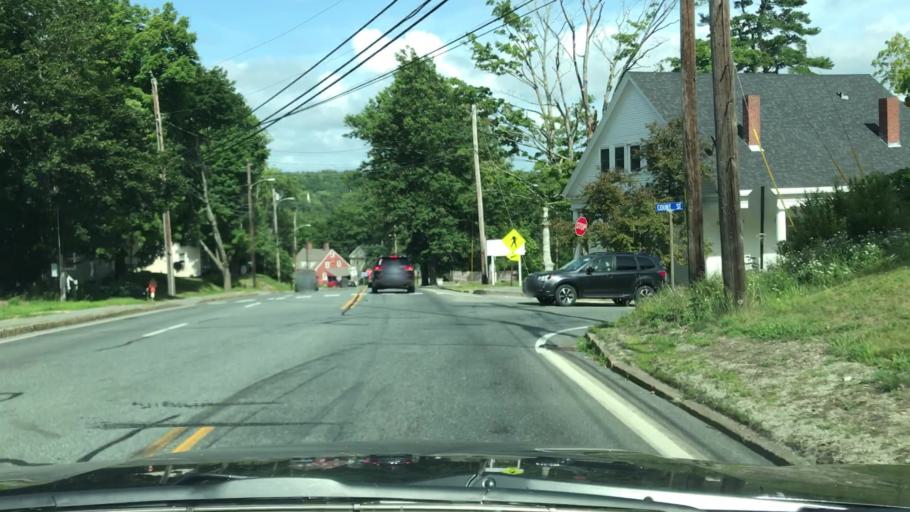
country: US
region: Maine
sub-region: Hancock County
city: Ellsworth
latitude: 44.5392
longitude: -68.4302
